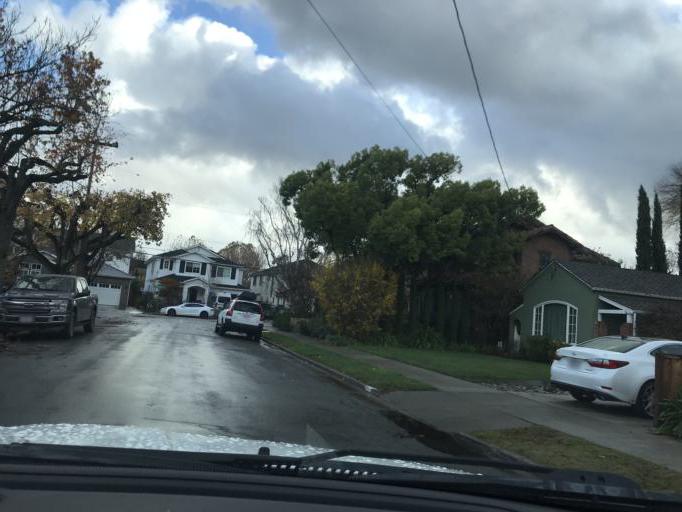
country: US
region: California
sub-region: Santa Clara County
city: Buena Vista
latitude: 37.3048
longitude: -121.9024
